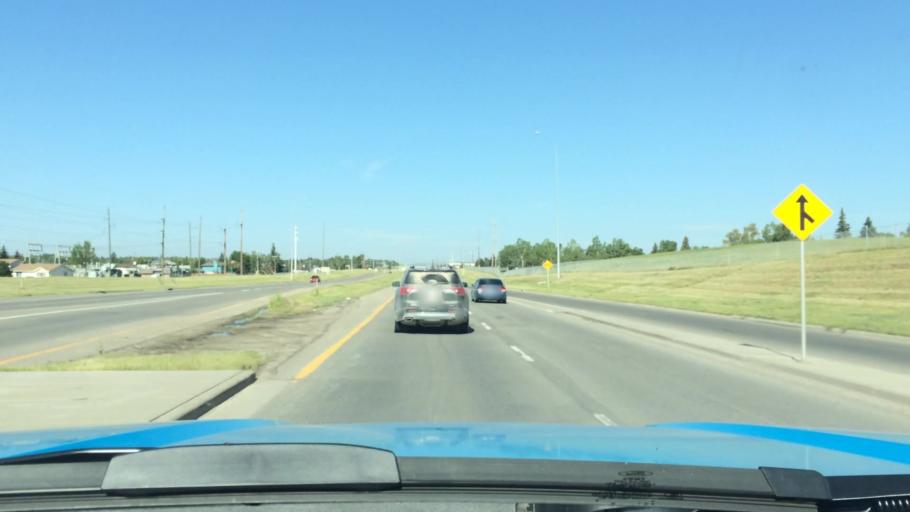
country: CA
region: Alberta
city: Chestermere
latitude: 51.0962
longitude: -113.9359
